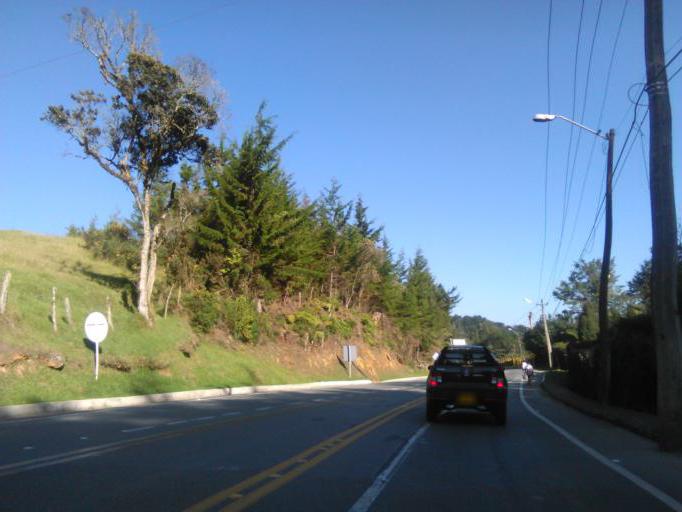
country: CO
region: Antioquia
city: Envigado
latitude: 6.1496
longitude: -75.5300
